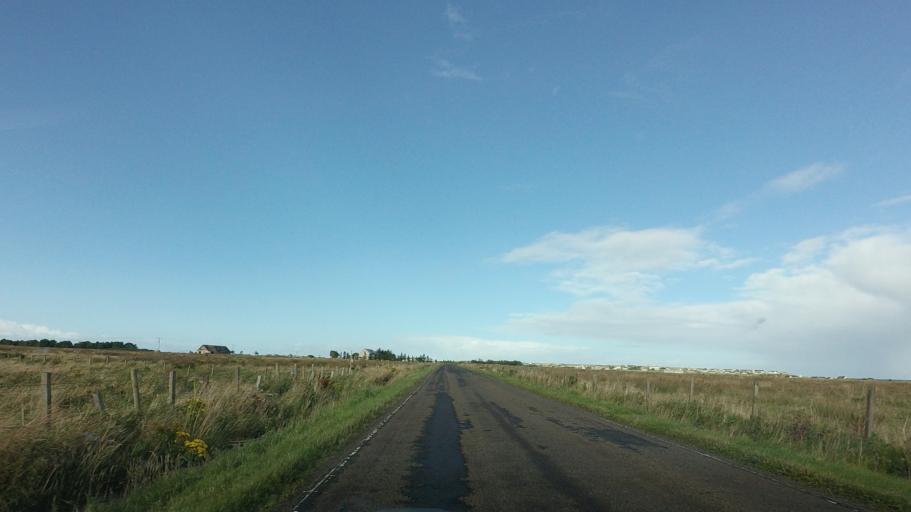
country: GB
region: Scotland
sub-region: Highland
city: Wick
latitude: 58.5226
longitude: -3.1412
